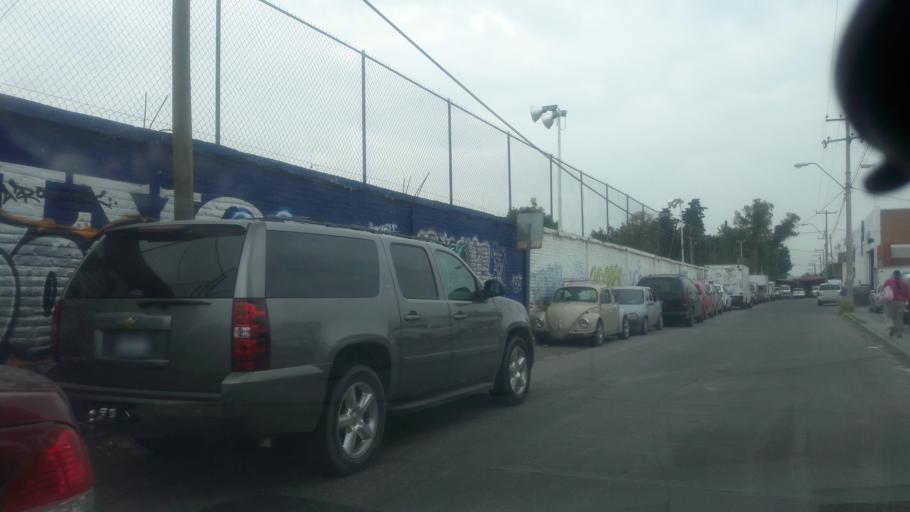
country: MX
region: Guanajuato
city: Leon
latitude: 21.1445
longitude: -101.6968
